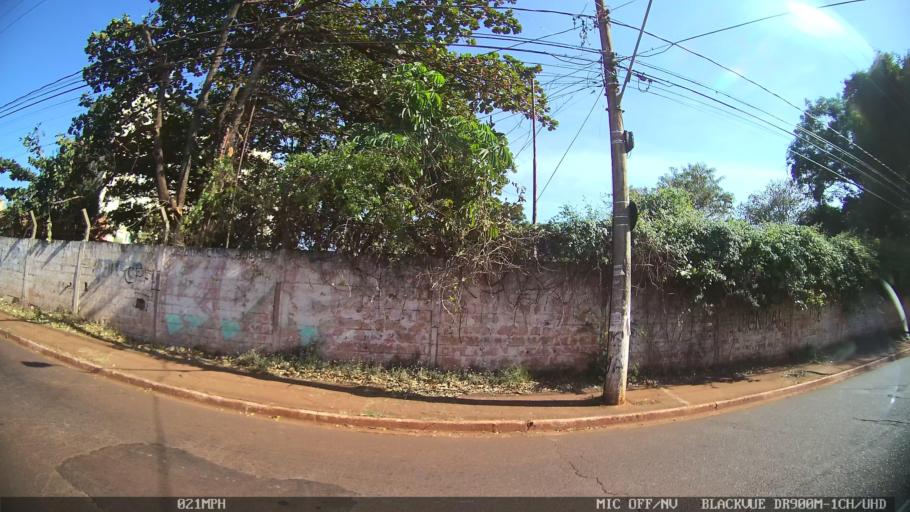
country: BR
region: Sao Paulo
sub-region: Ribeirao Preto
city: Ribeirao Preto
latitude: -21.1789
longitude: -47.7775
